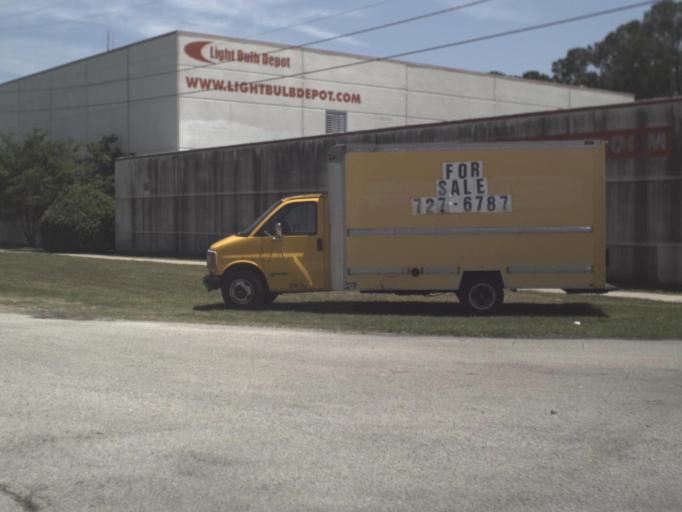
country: US
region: Florida
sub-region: Duval County
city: Jacksonville
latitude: 30.2892
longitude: -81.5845
